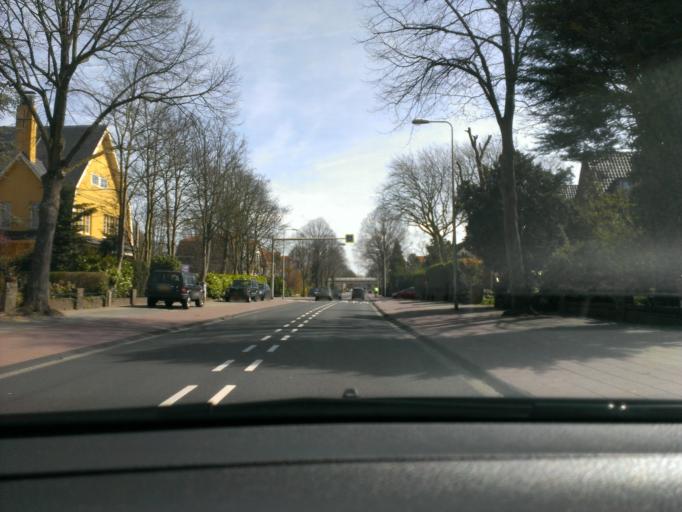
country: NL
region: North Holland
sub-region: Gemeente Bloemendaal
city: Bloemendaal
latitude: 52.3913
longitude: 4.6141
